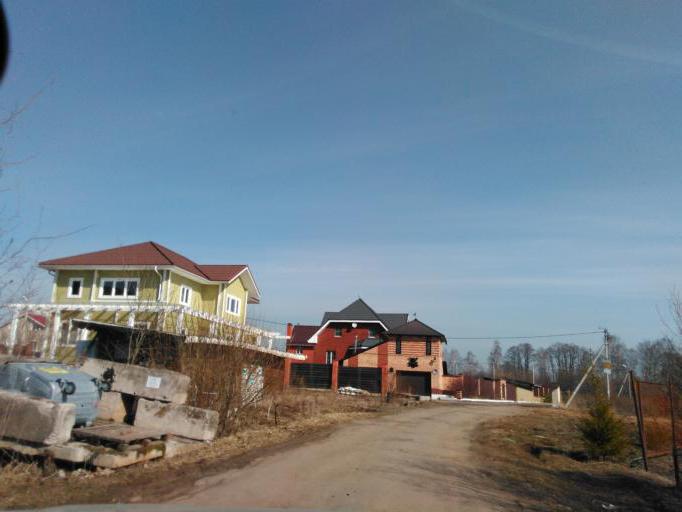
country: RU
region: Moskovskaya
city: Opalikha
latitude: 55.8737
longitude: 37.2509
